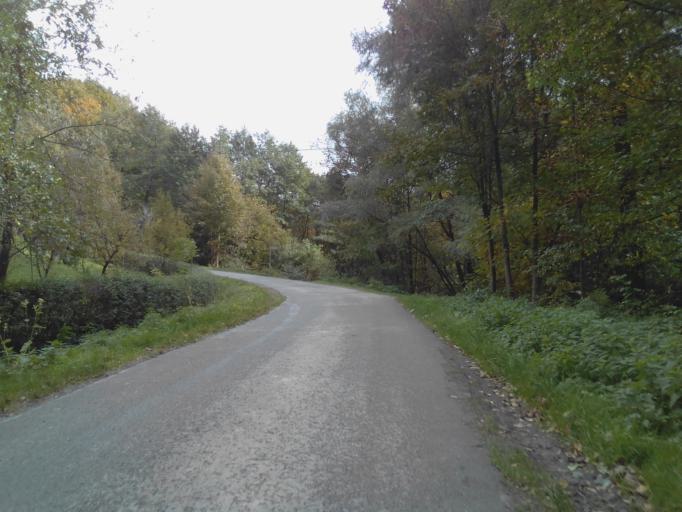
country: PL
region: Subcarpathian Voivodeship
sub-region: Powiat strzyzowski
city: Gwoznica Gorna
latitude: 49.8334
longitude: 22.0029
